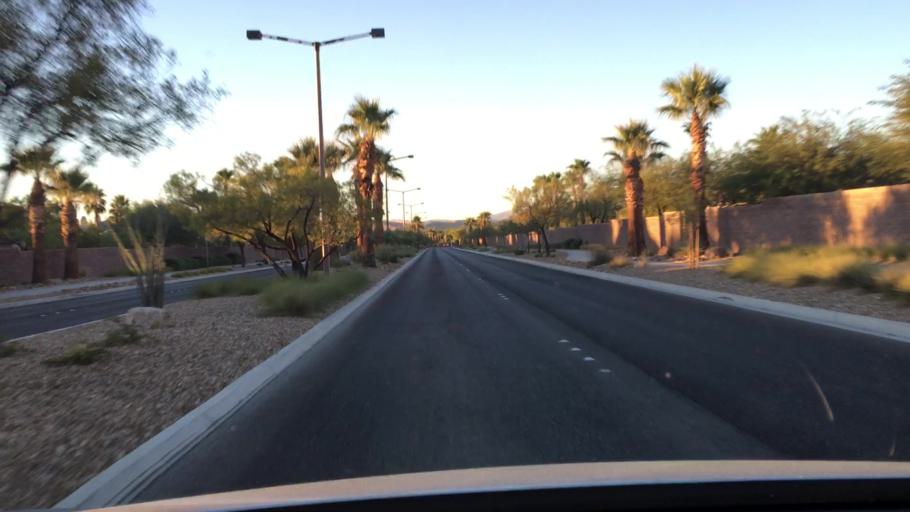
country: US
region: Nevada
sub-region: Clark County
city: Summerlin South
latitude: 36.1390
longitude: -115.3425
